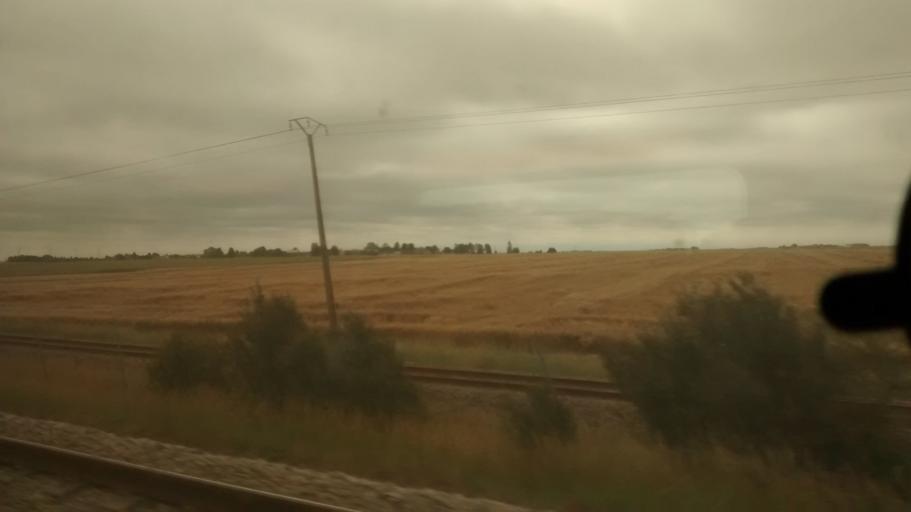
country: FR
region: Centre
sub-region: Departement d'Eure-et-Loir
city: Bonneval
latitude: 48.2260
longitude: 1.4633
